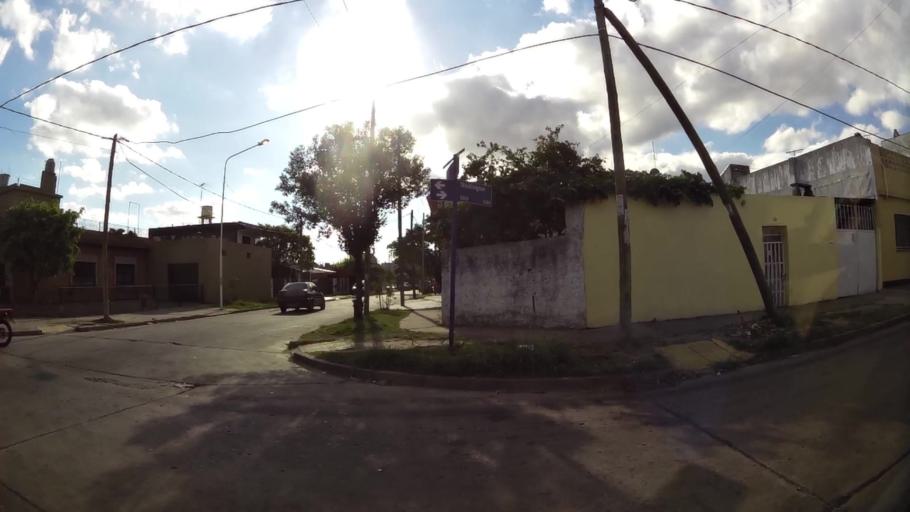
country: AR
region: Buenos Aires
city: San Justo
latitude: -34.6945
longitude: -58.5902
